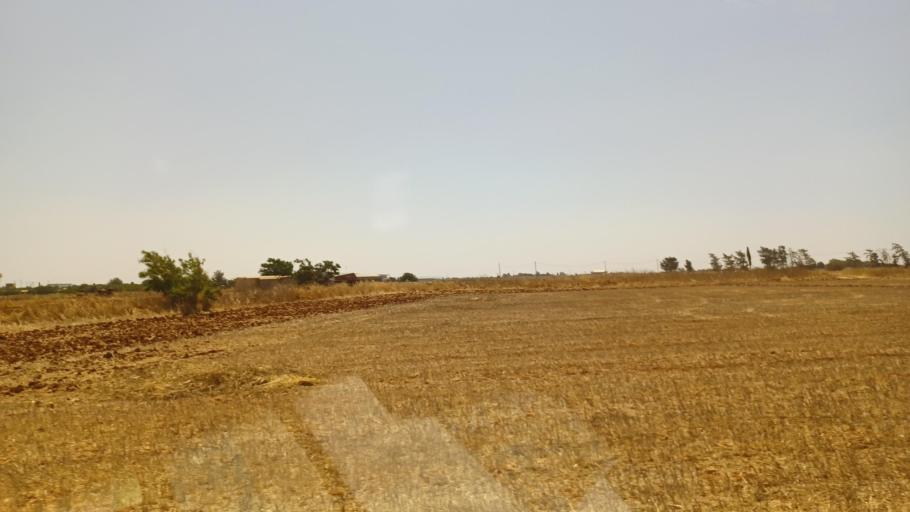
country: CY
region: Ammochostos
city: Achna
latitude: 35.0291
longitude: 33.8056
